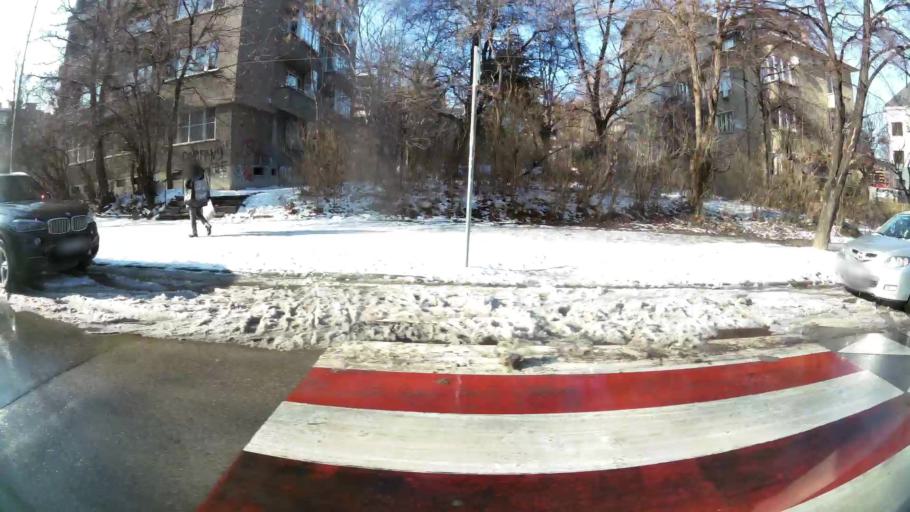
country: BG
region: Sofia-Capital
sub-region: Stolichna Obshtina
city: Sofia
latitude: 42.6746
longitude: 23.3562
